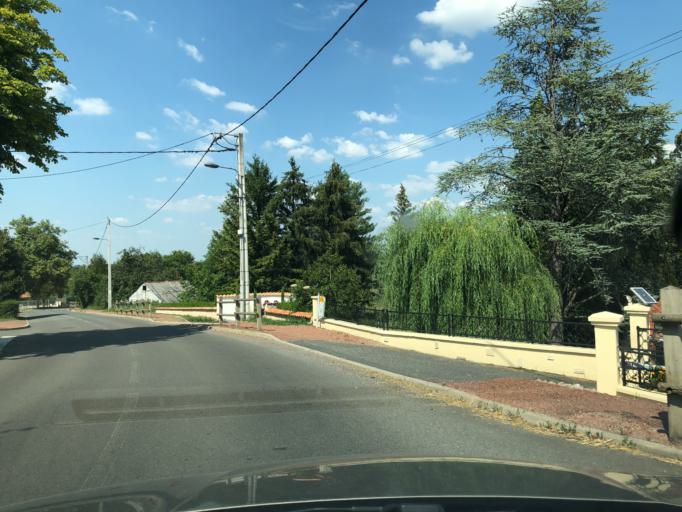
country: FR
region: Auvergne
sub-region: Departement de l'Allier
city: Cusset
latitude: 46.1171
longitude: 3.4666
